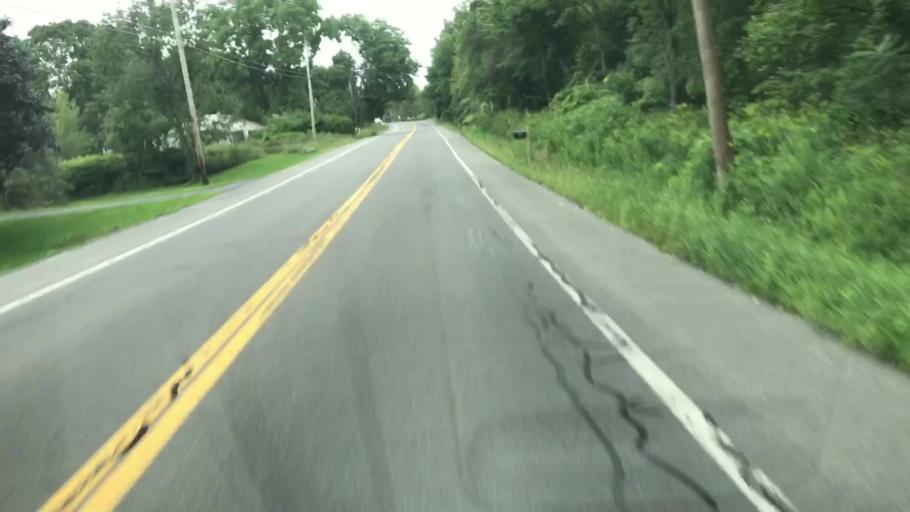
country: US
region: New York
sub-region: Onondaga County
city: Camillus
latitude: 43.0586
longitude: -76.3189
